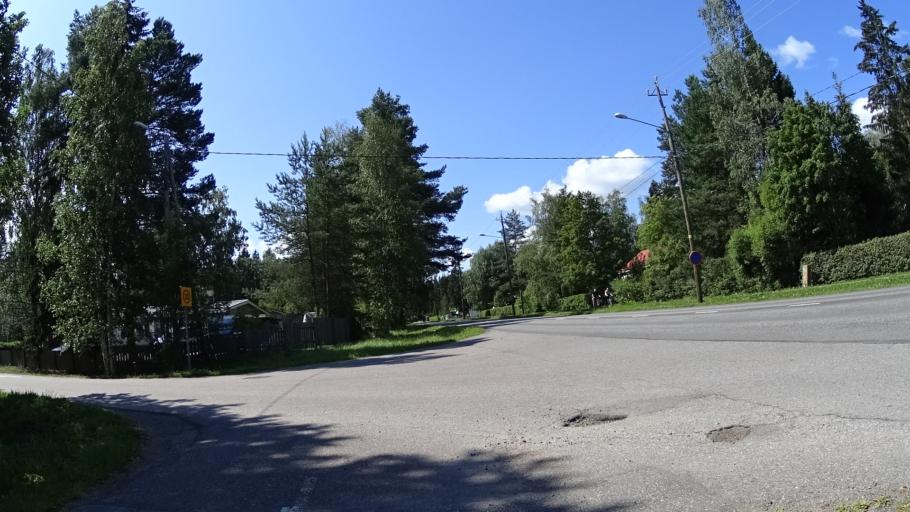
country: FI
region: Uusimaa
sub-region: Helsinki
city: Jaervenpaeae
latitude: 60.4684
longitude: 25.0703
